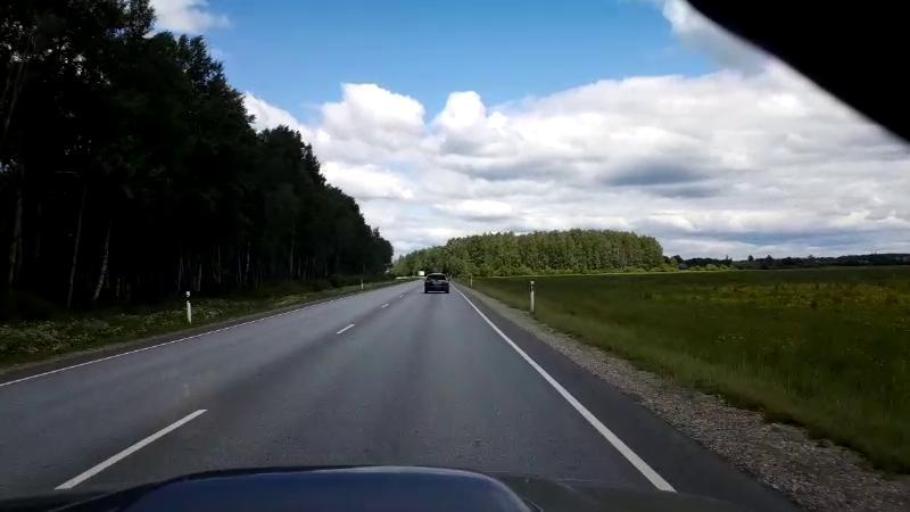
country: EE
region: Paernumaa
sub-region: Sauga vald
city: Sauga
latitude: 58.4709
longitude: 24.5248
